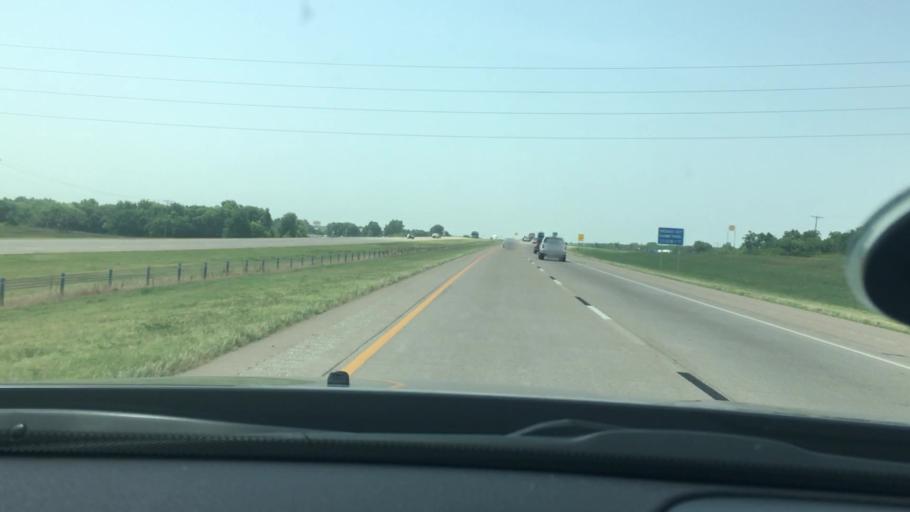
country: US
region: Oklahoma
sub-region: Garvin County
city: Wynnewood
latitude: 34.6573
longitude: -97.2211
